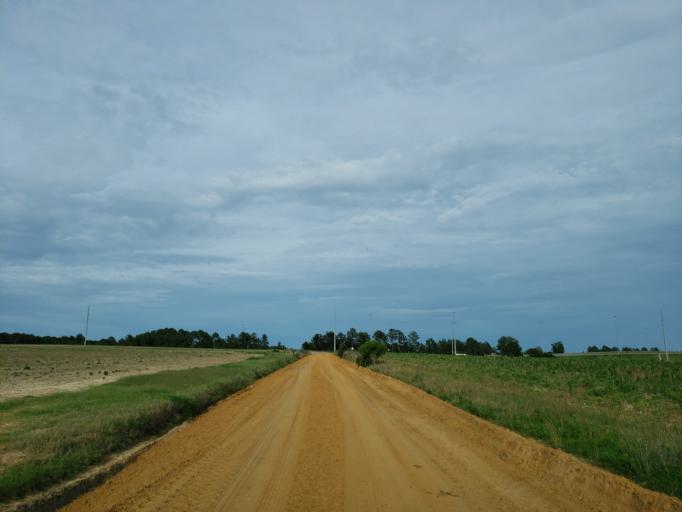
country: US
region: Georgia
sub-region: Dooly County
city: Vienna
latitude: 32.1278
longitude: -83.7648
